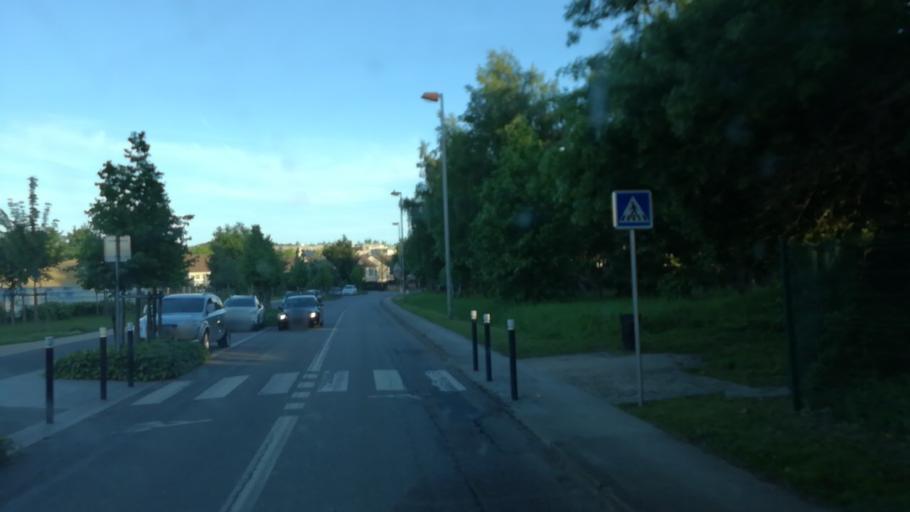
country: FR
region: Ile-de-France
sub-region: Departement des Yvelines
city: Elancourt
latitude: 48.7714
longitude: 1.9617
